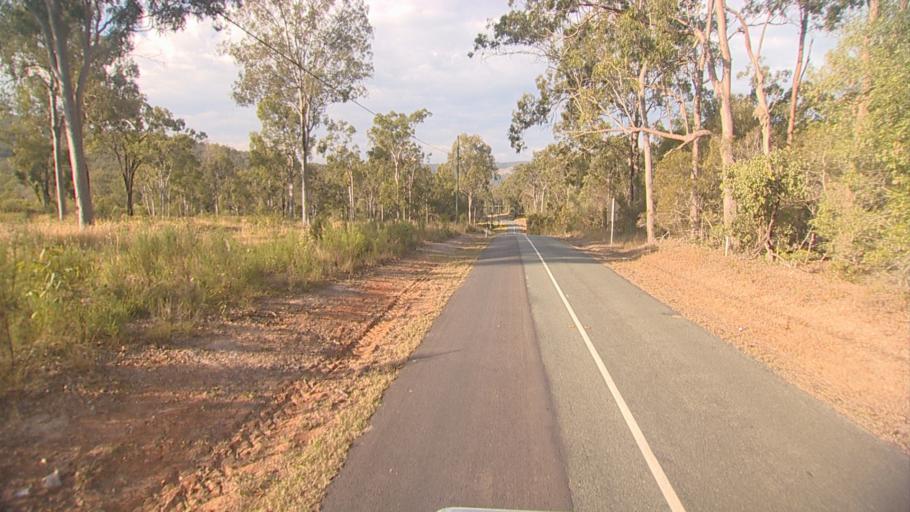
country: AU
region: Queensland
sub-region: Gold Coast
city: Ormeau Hills
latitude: -27.8451
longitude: 153.1512
